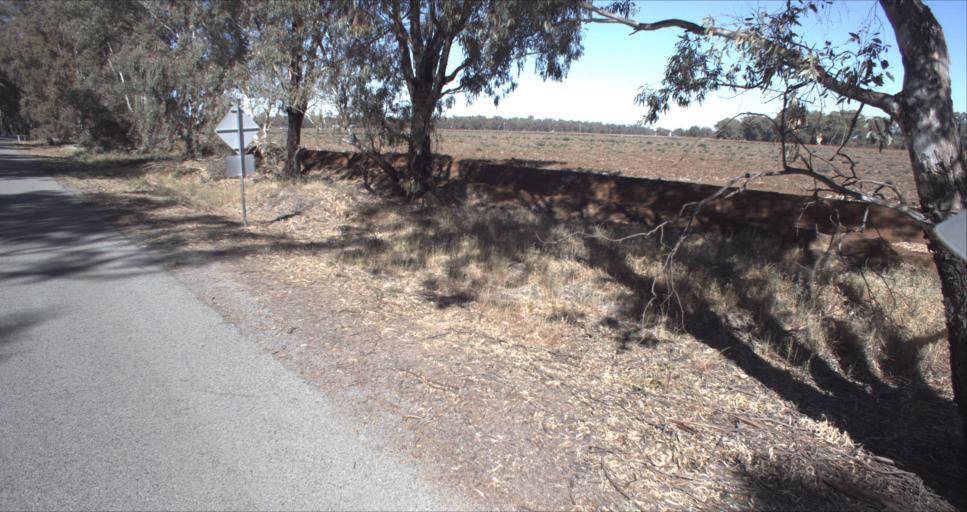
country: AU
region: New South Wales
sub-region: Leeton
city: Leeton
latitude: -34.6062
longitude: 146.2635
